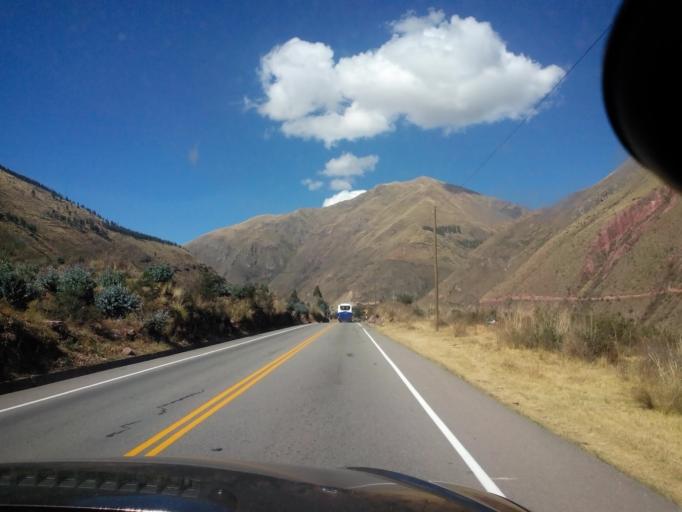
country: PE
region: Cusco
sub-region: Provincia de Quispicanchis
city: Cusipata
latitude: -13.9689
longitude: -71.4945
